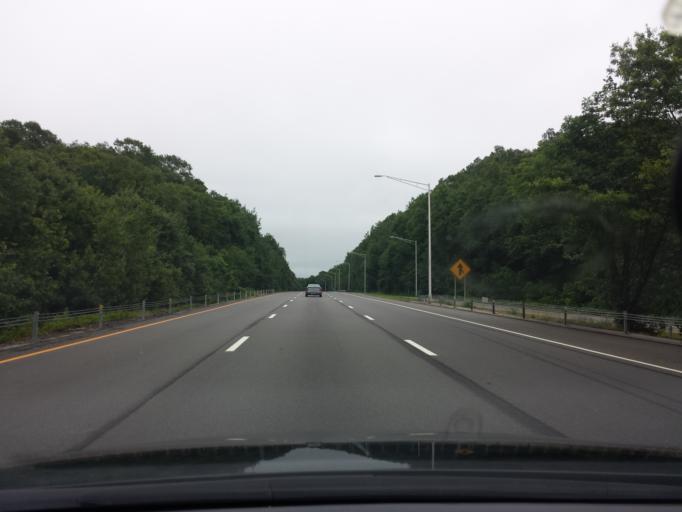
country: US
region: Connecticut
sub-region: New London County
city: Poquonock Bridge
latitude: 41.3616
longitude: -72.0249
